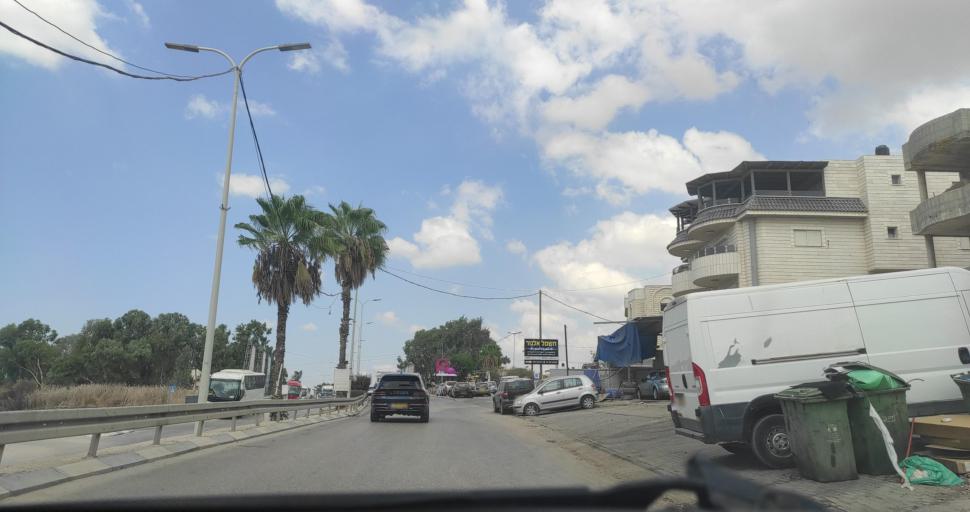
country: IL
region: Central District
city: Kafr Qasim
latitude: 32.1156
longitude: 34.9639
